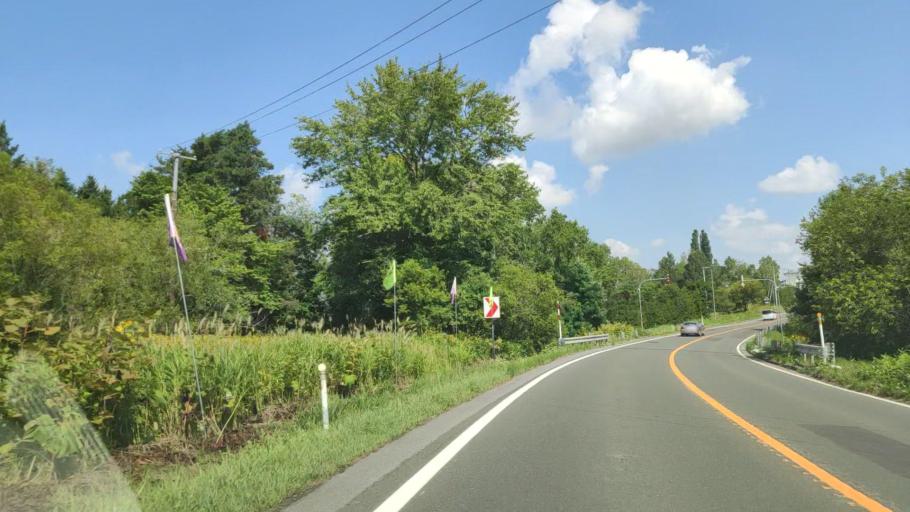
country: JP
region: Hokkaido
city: Shimo-furano
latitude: 43.5152
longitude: 142.4469
